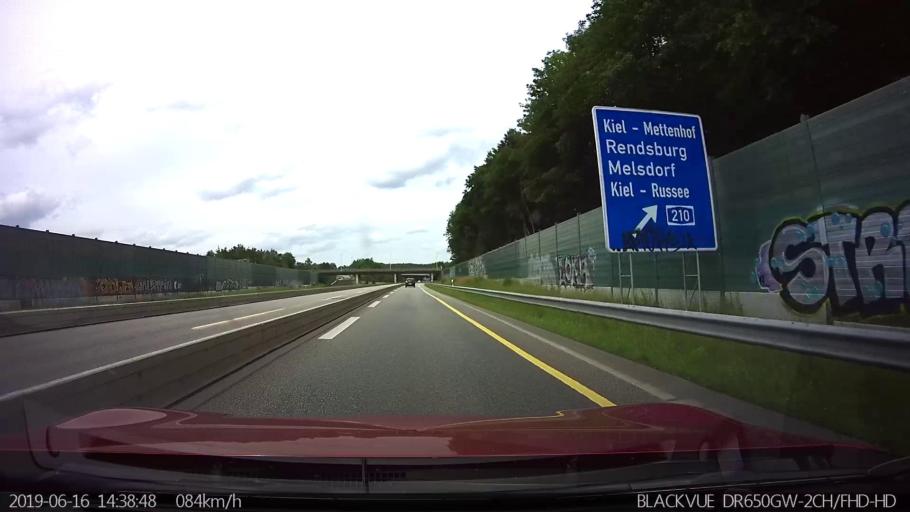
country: DE
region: Schleswig-Holstein
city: Mielkendorf
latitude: 54.2987
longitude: 10.0511
